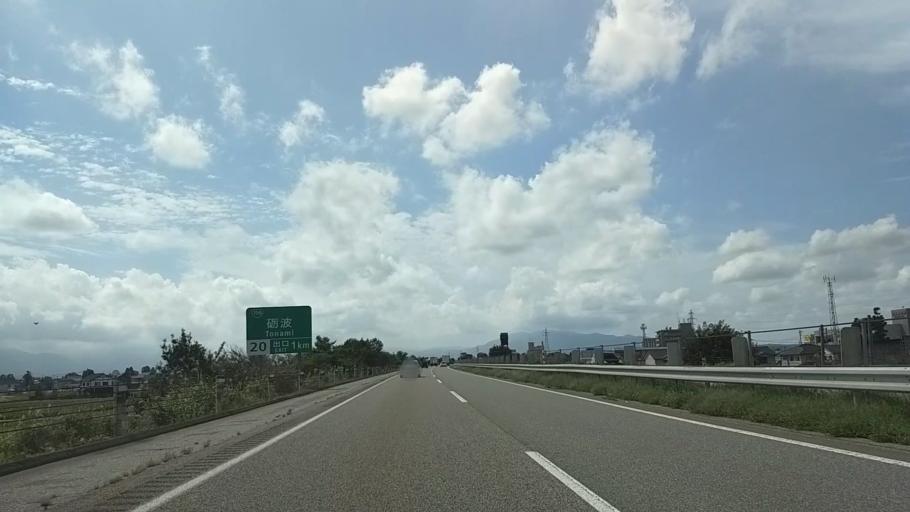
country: JP
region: Toyama
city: Nanto-shi
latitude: 36.6304
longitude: 136.9645
